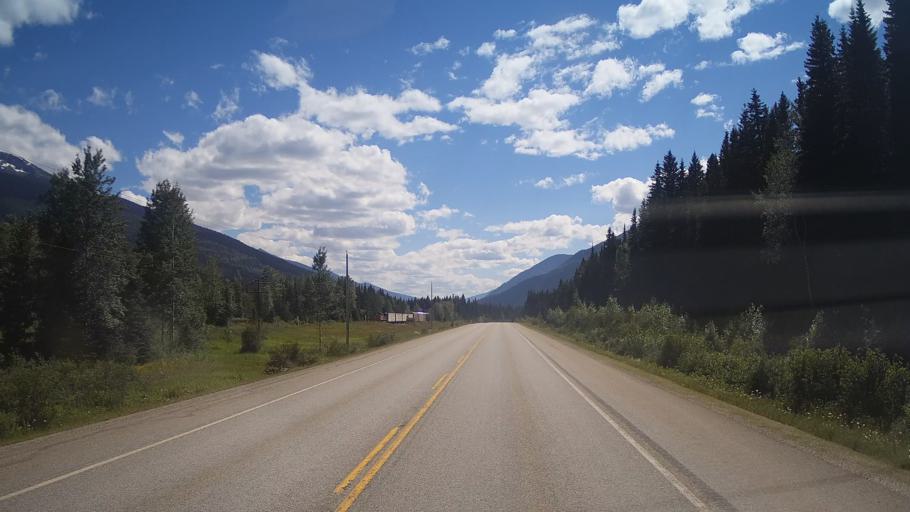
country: CA
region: Alberta
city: Jasper Park Lodge
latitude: 52.5779
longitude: -119.0971
